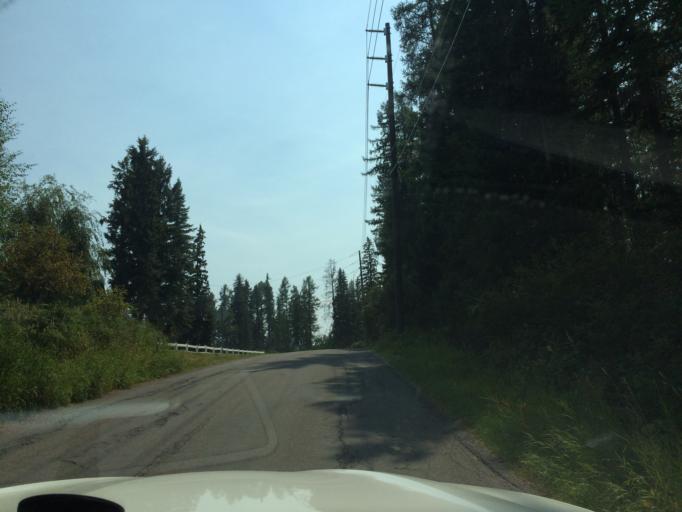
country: US
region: Montana
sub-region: Flathead County
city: Whitefish
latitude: 48.4009
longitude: -114.3273
